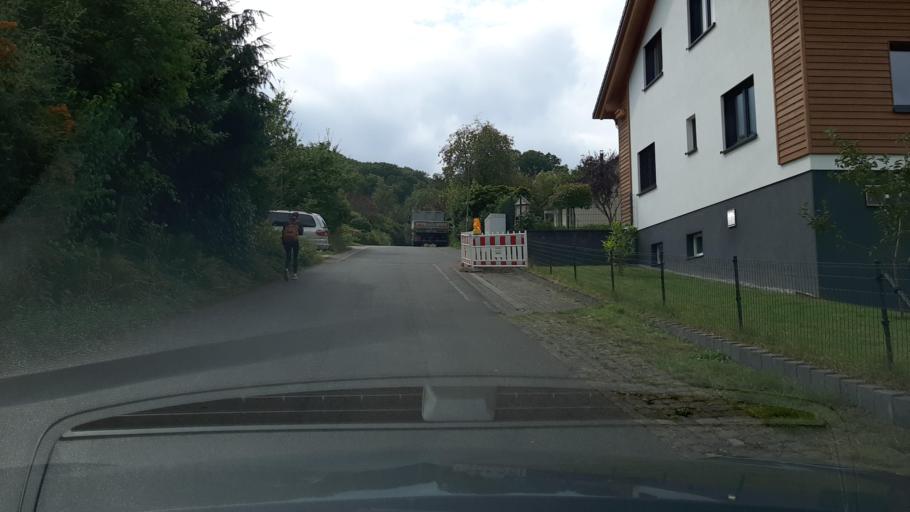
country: DE
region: Rheinland-Pfalz
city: Alf
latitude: 50.0515
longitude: 7.1257
